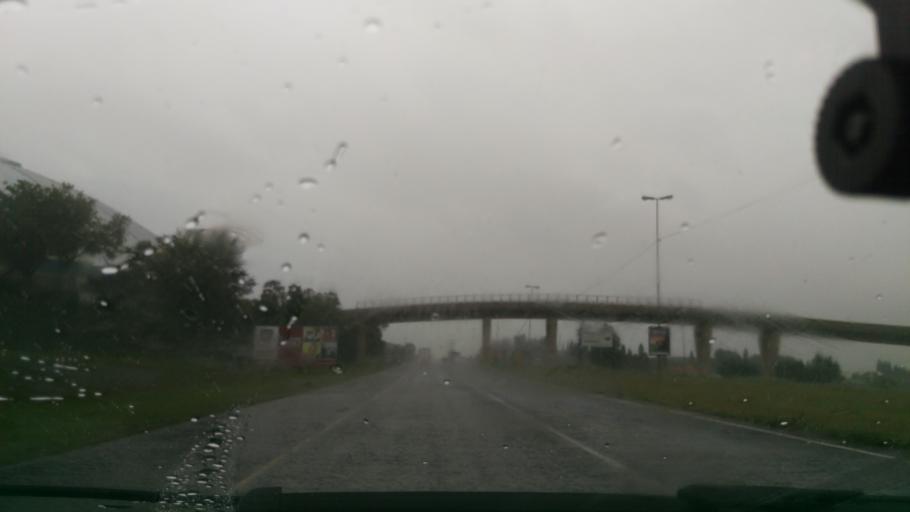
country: ZA
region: Gauteng
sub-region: West Rand District Municipality
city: Muldersdriseloop
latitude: -26.0614
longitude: 27.9428
